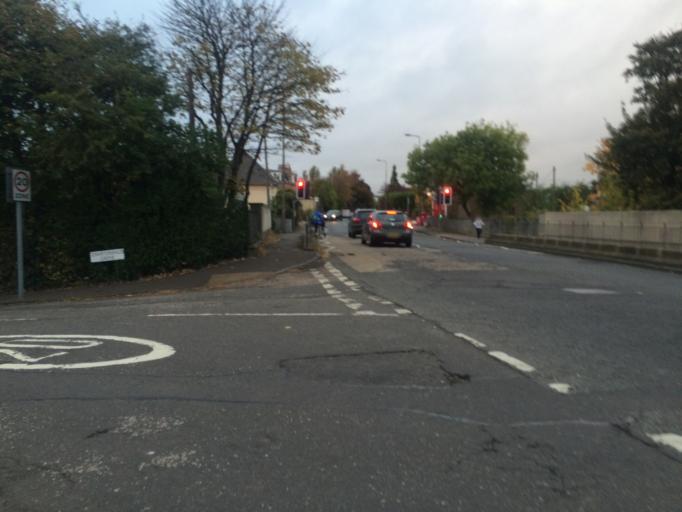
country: GB
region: Scotland
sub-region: Edinburgh
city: Edinburgh
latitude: 55.9270
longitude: -3.1868
